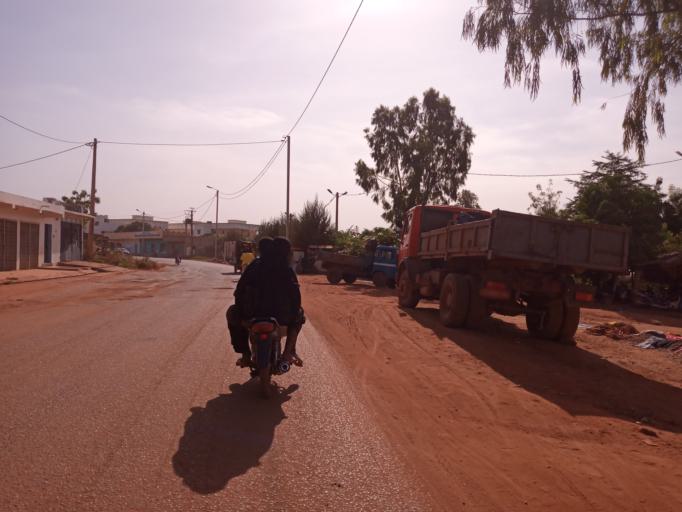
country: ML
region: Bamako
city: Bamako
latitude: 12.6271
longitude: -7.9546
